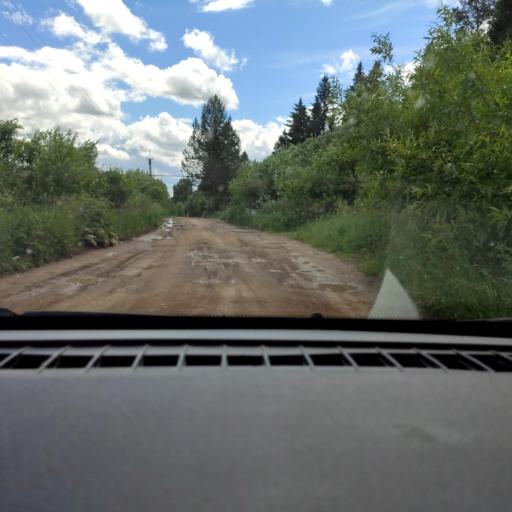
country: RU
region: Perm
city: Overyata
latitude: 58.1372
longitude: 55.8228
